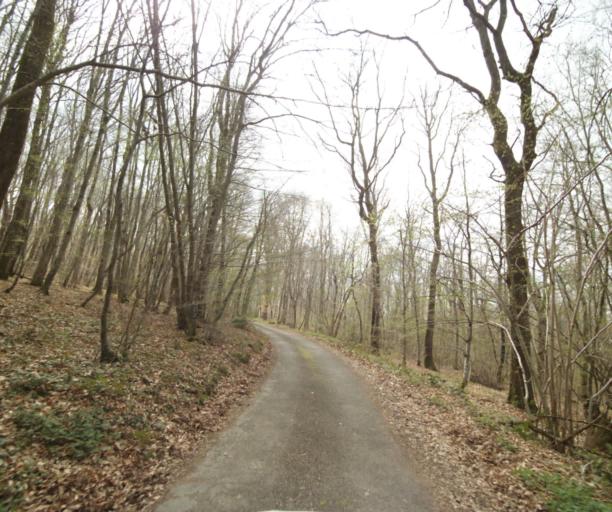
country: FR
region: Bourgogne
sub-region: Departement de Saone-et-Loire
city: Charolles
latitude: 46.3892
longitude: 4.2716
